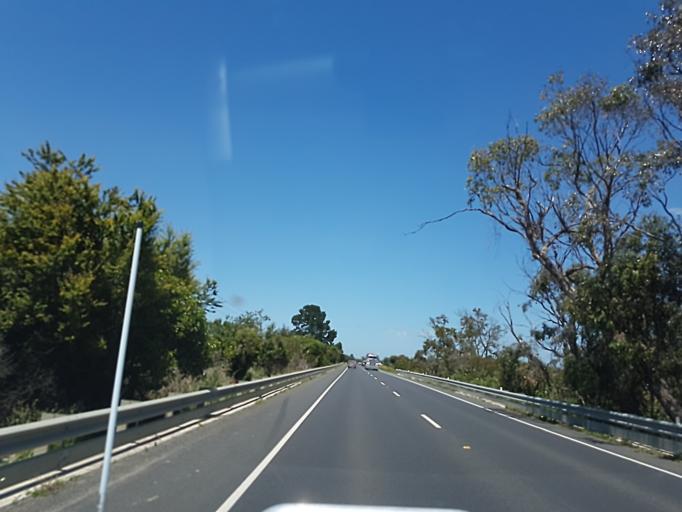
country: AU
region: Victoria
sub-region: Cardinia
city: Pakenham South
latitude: -38.1309
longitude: 145.4897
